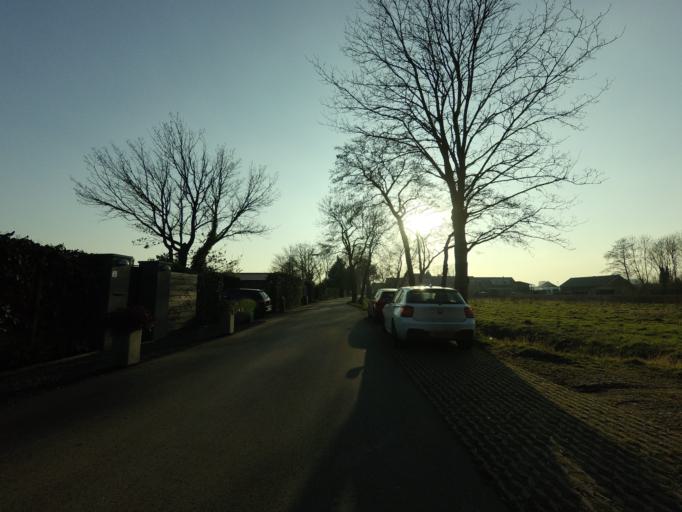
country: NL
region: North Holland
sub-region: Gemeente Haarlem
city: Haarlem
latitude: 52.3801
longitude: 4.6787
